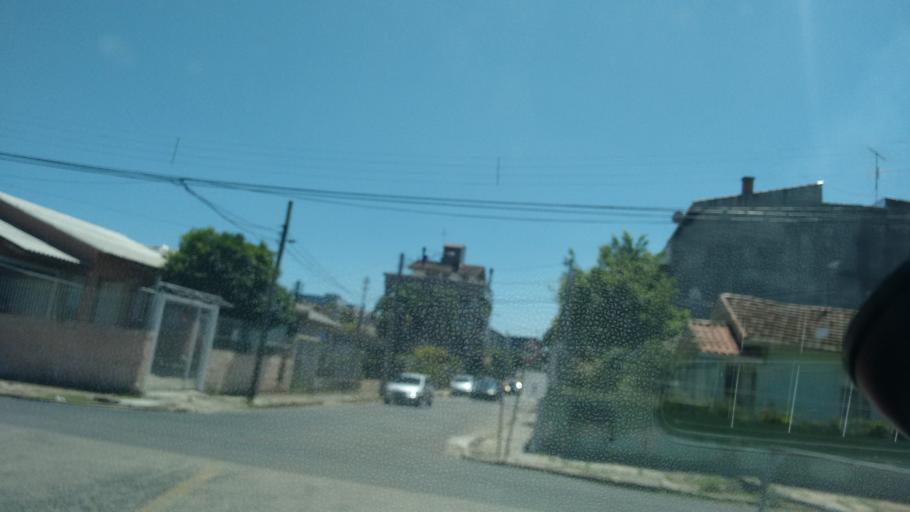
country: BR
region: Rio Grande do Sul
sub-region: Cachoeirinha
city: Cachoeirinha
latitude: -29.9971
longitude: -51.1285
